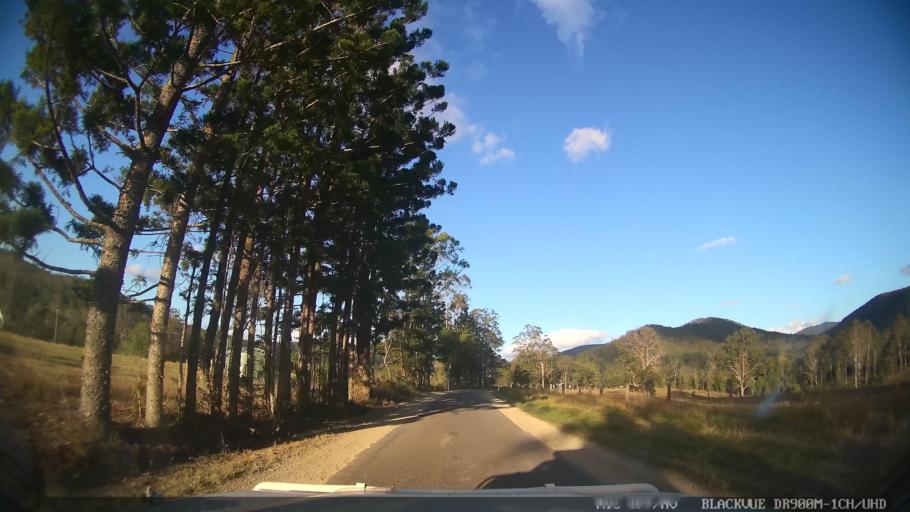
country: AU
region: Queensland
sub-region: Sunshine Coast
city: Nambour
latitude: -26.6284
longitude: 152.6836
